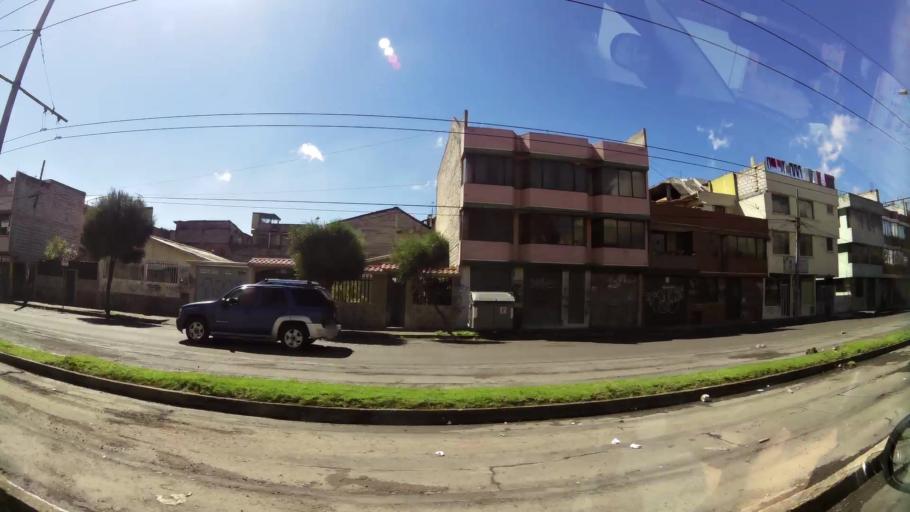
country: EC
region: Pichincha
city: Quito
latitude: -0.2671
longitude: -78.5322
